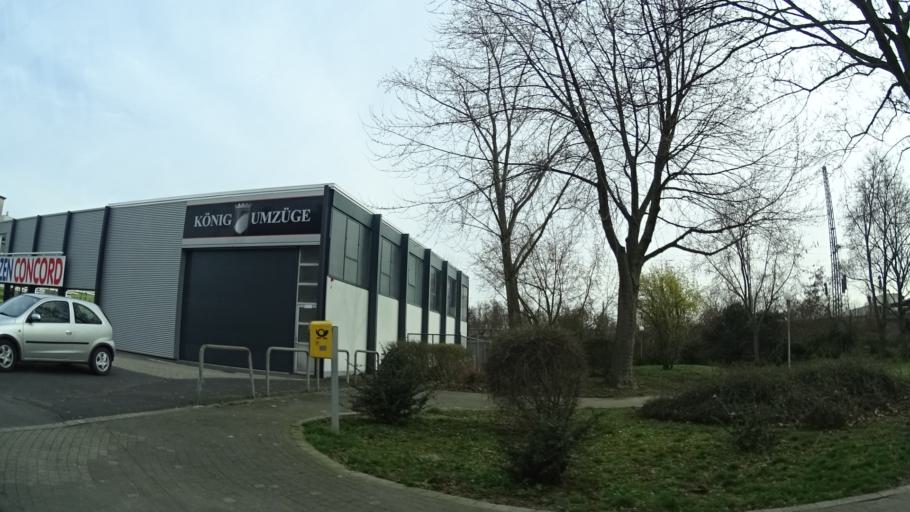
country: DE
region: Rheinland-Pfalz
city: Neustadt
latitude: 49.3511
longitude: 8.1516
